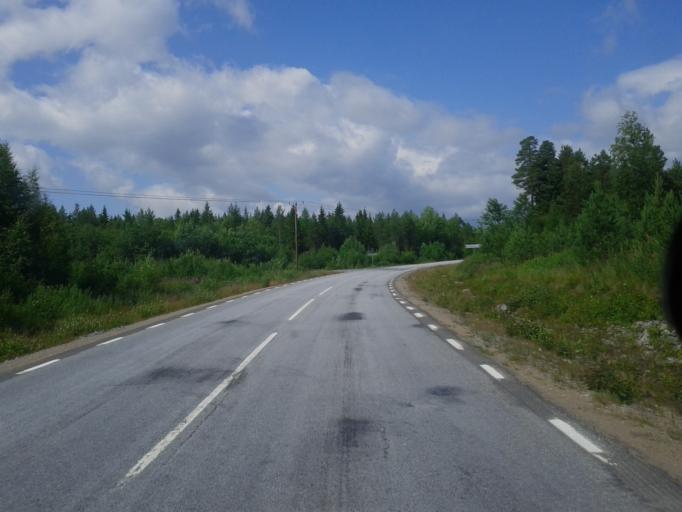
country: SE
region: Vaesterbotten
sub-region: Nordmalings Kommun
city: Nordmaling
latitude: 63.5796
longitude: 19.4590
